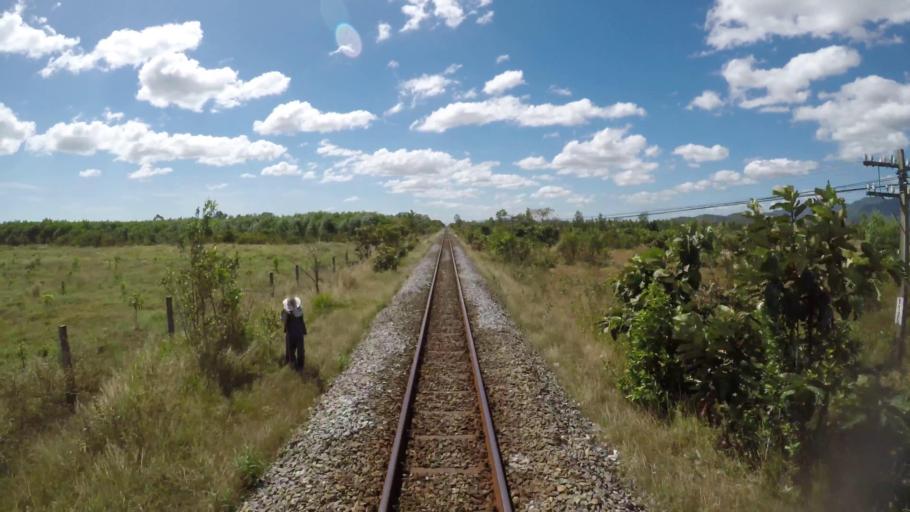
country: VN
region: Binh Thuan
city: Ma Lam
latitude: 11.0277
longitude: 108.0675
